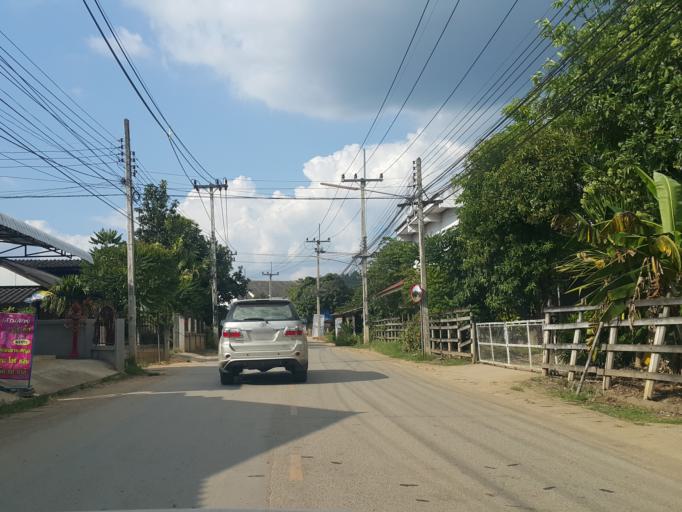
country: TH
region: Chiang Mai
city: Mae Chaem
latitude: 18.5086
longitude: 98.3600
